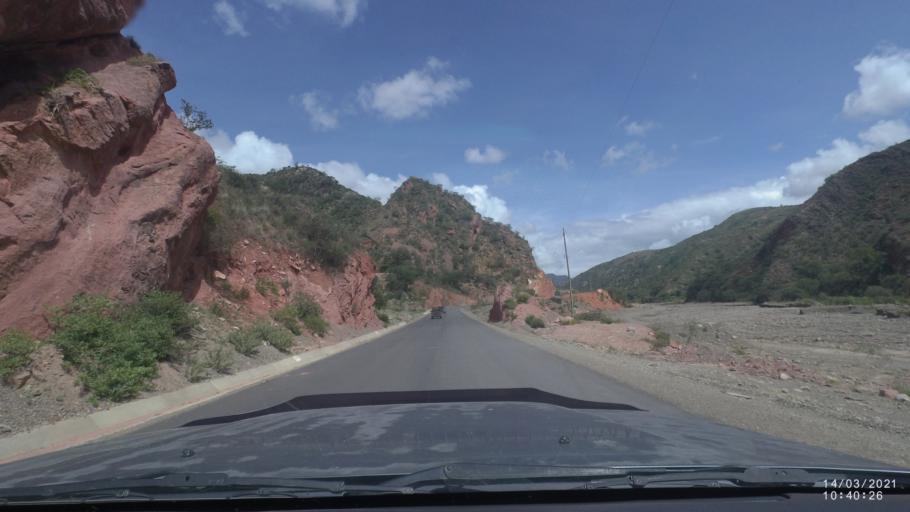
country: BO
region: Cochabamba
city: Cliza
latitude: -17.8823
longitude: -65.9035
